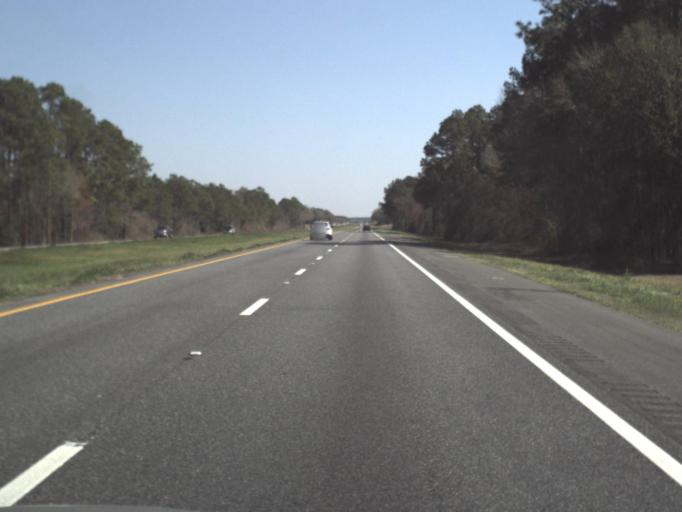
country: US
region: Florida
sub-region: Jackson County
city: Marianna
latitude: 30.7024
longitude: -85.1391
